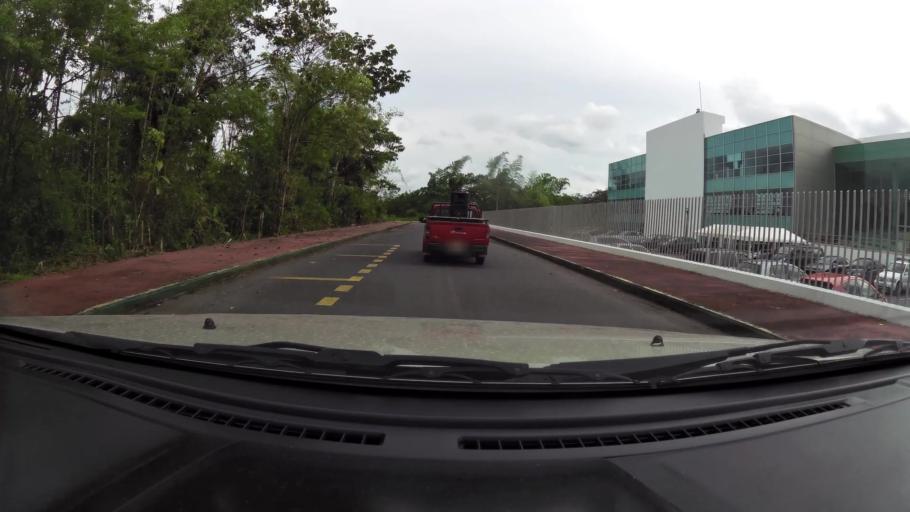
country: EC
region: Pastaza
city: Puyo
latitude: -1.5025
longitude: -78.0201
